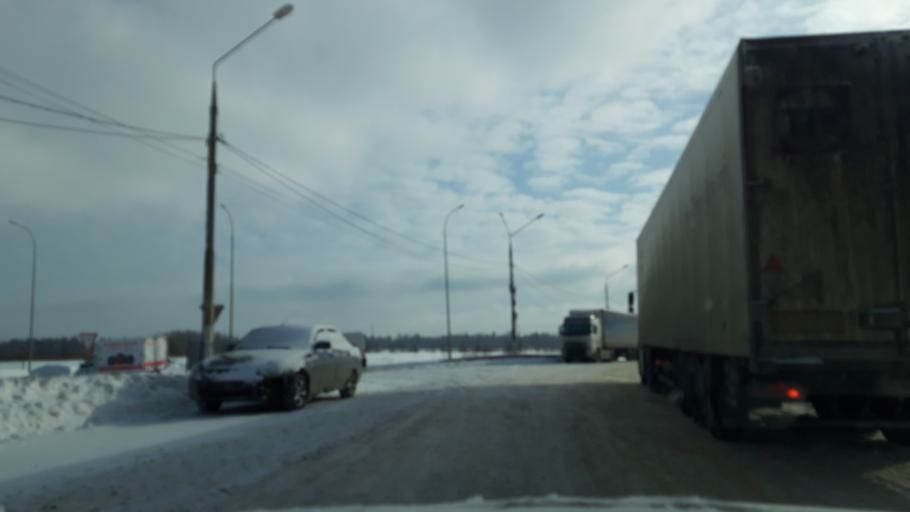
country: RU
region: Moskovskaya
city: Yermolino
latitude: 56.1420
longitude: 37.3797
